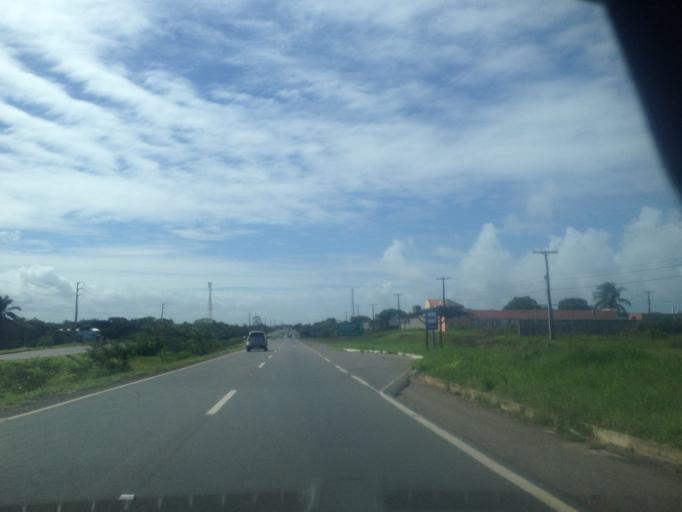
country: BR
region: Bahia
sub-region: Camacari
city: Camacari
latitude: -12.6576
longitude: -38.0883
